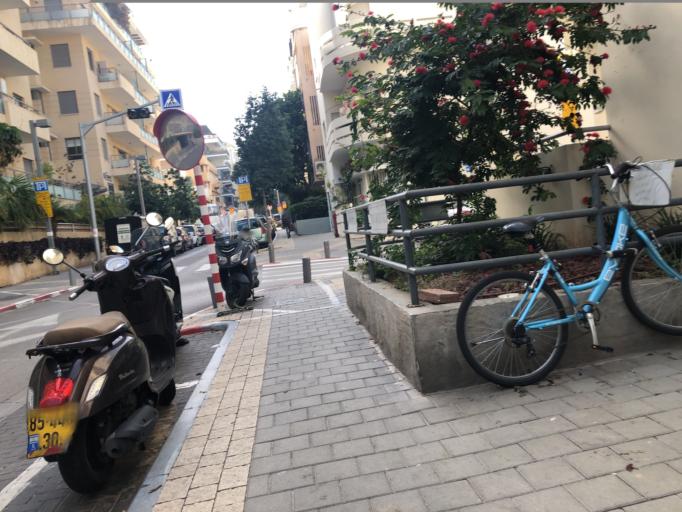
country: IL
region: Tel Aviv
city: Tel Aviv
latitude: 32.0694
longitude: 34.7760
